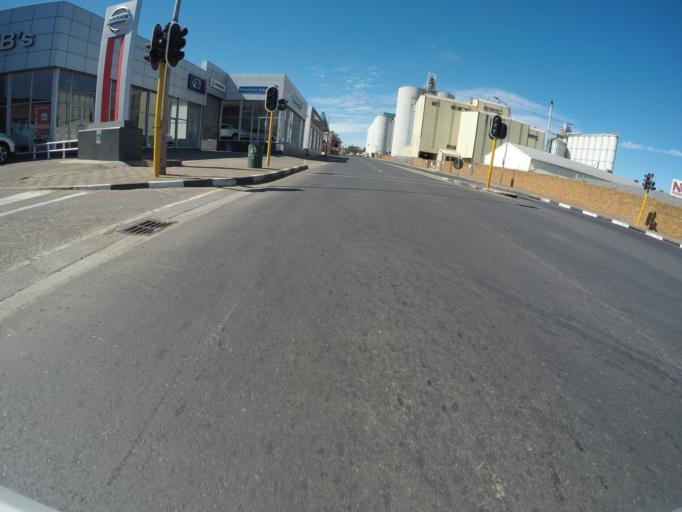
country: ZA
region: Western Cape
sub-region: West Coast District Municipality
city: Malmesbury
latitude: -33.4659
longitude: 18.7195
